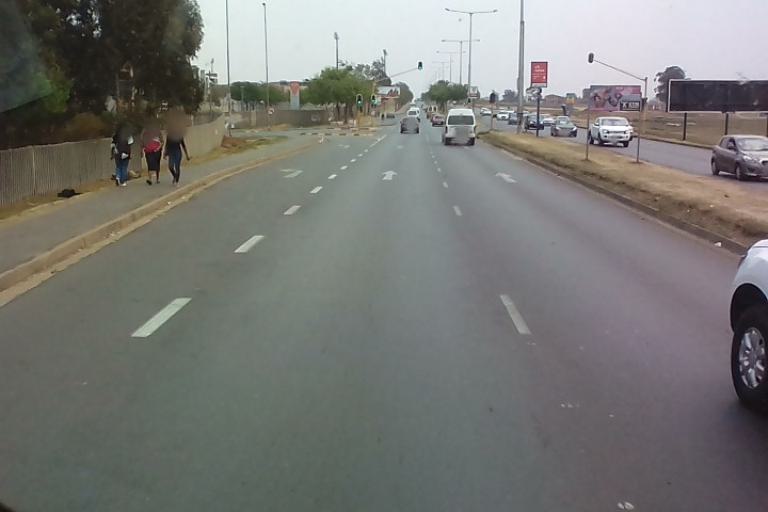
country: ZA
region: Gauteng
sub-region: City of Johannesburg Metropolitan Municipality
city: Soweto
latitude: -26.2596
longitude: 27.9255
